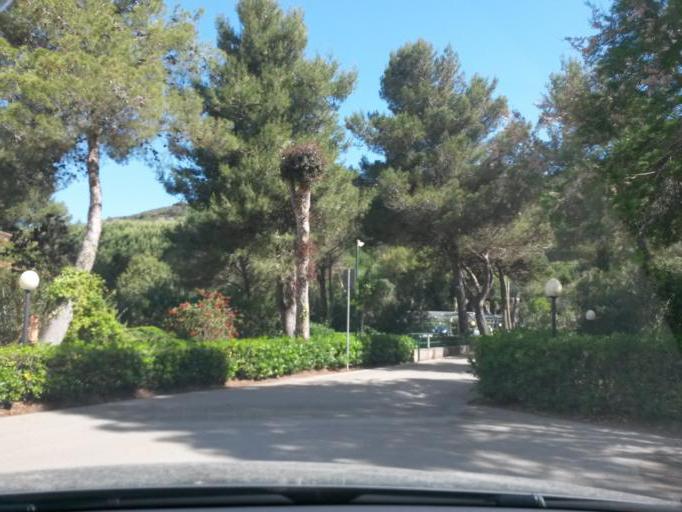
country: IT
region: Tuscany
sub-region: Provincia di Livorno
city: Rio Marina
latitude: 42.7947
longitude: 10.4251
